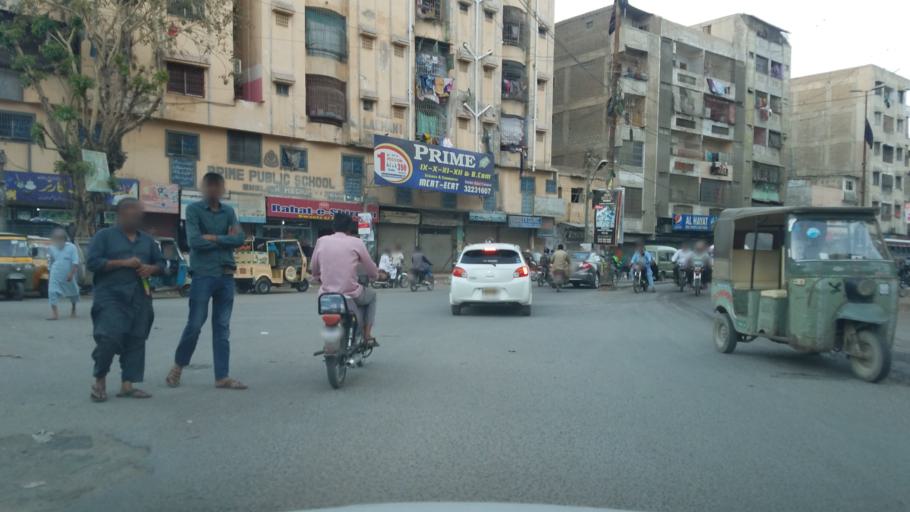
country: PK
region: Sindh
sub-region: Karachi District
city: Karachi
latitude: 24.8736
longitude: 67.0289
